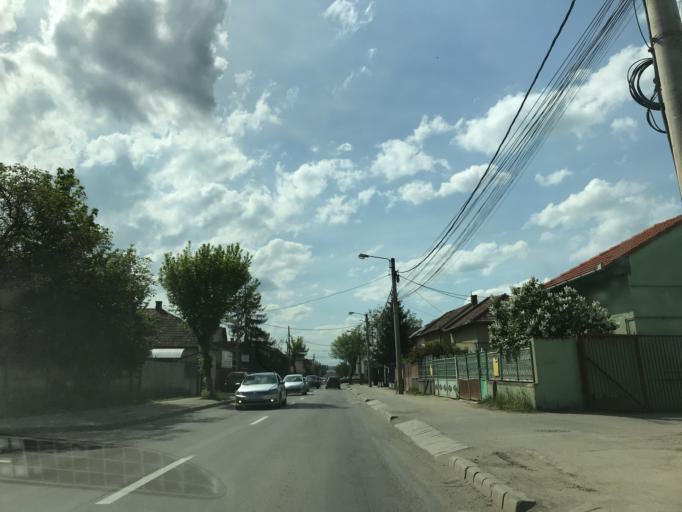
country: RO
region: Cluj
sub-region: Municipiul Cluj-Napoca
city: Cluj-Napoca
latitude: 46.7873
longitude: 23.6335
